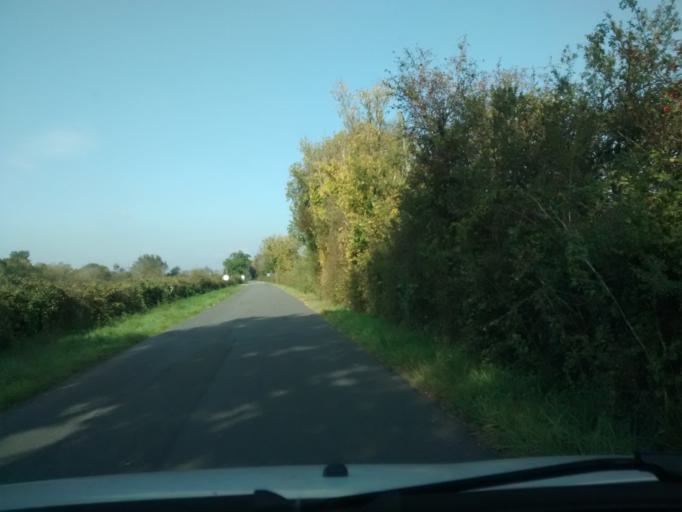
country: FR
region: Pays de la Loire
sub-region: Departement de la Loire-Atlantique
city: Vue
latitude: 47.2440
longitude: -1.8842
